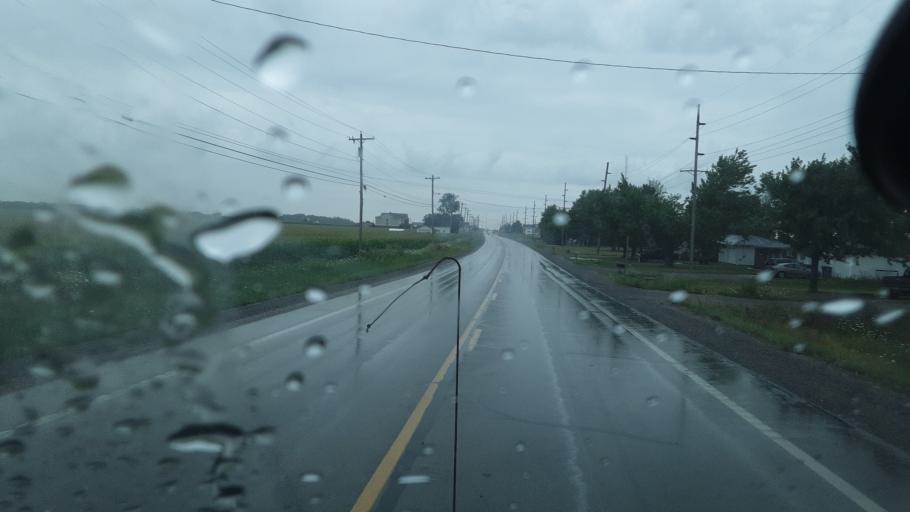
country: US
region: Ohio
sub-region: Williams County
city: Montpelier
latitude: 41.6009
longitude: -84.5558
